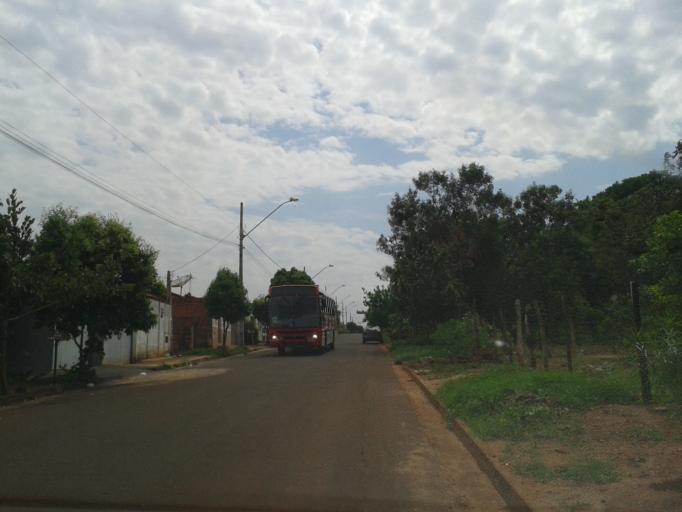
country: BR
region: Minas Gerais
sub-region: Ituiutaba
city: Ituiutaba
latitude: -18.9877
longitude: -49.4382
